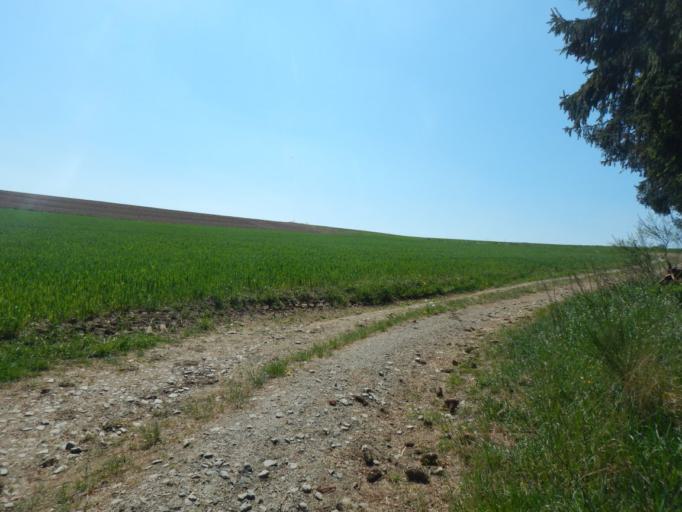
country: LU
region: Diekirch
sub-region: Canton de Clervaux
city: Troisvierges
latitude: 50.1391
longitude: 6.0138
